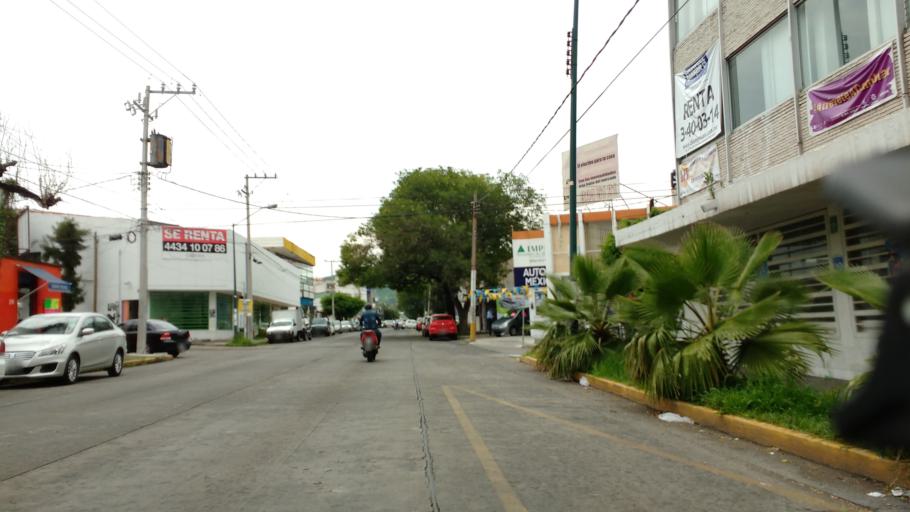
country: MX
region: Michoacan
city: Morelia
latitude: 19.6942
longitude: -101.1717
